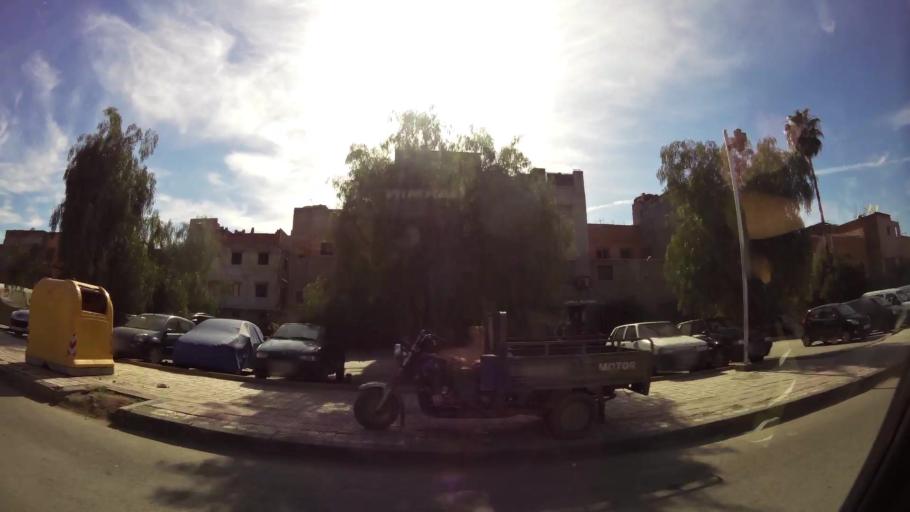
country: MA
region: Marrakech-Tensift-Al Haouz
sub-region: Marrakech
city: Marrakesh
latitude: 31.6099
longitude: -7.9574
